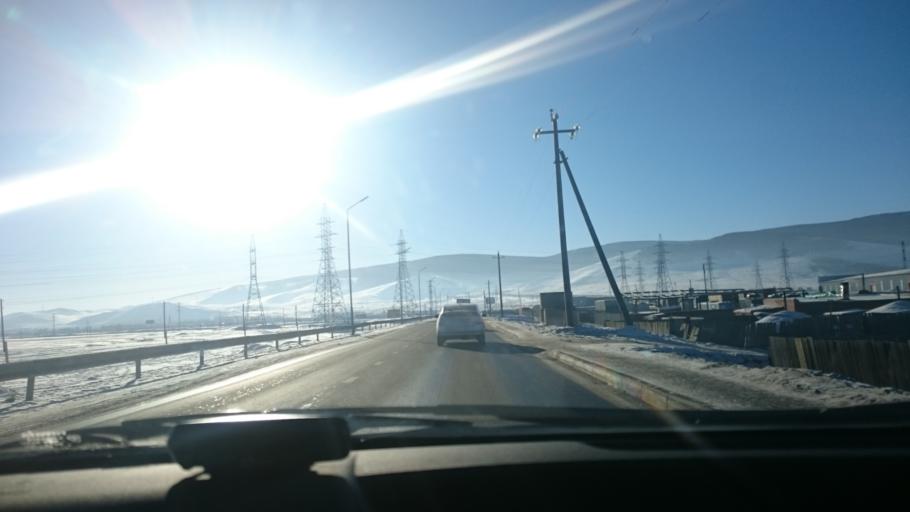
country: MN
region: Ulaanbaatar
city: Ulaanbaatar
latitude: 47.9046
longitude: 107.0349
